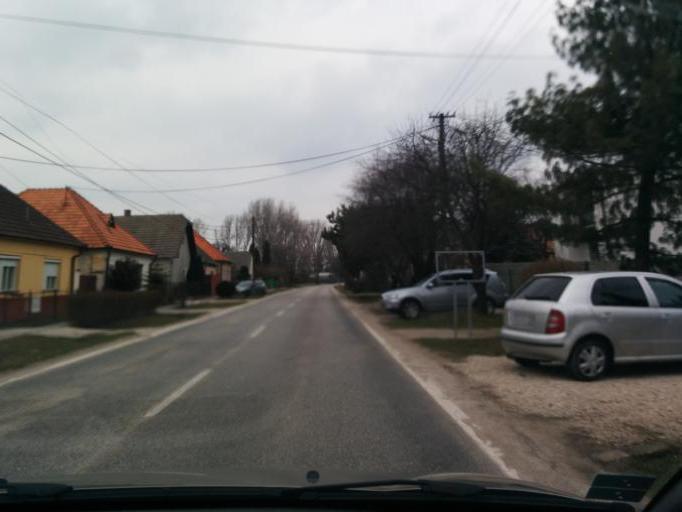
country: SK
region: Trnavsky
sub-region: Okres Galanta
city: Galanta
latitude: 48.2573
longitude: 17.8094
